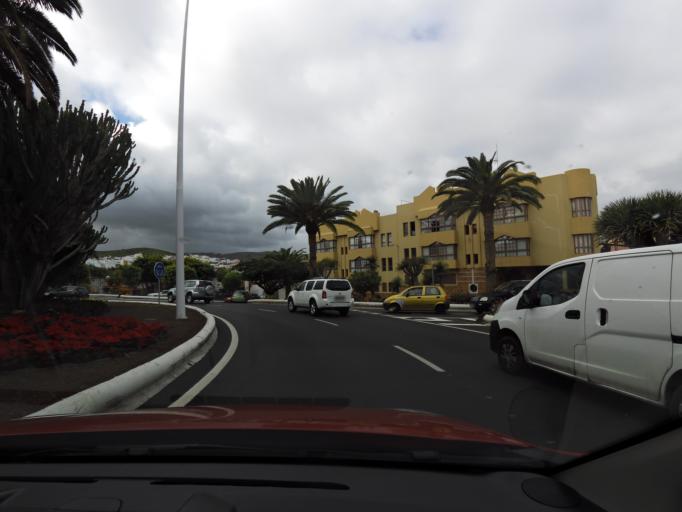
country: ES
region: Canary Islands
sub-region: Provincia de Las Palmas
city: Telde
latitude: 27.9993
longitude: -15.4198
